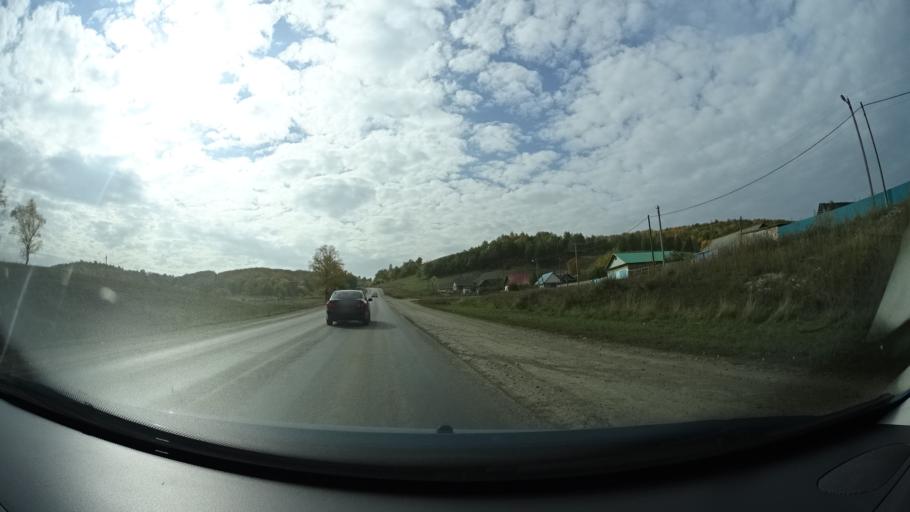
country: RU
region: Bashkortostan
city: Tuymazy
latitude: 54.5518
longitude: 53.5890
